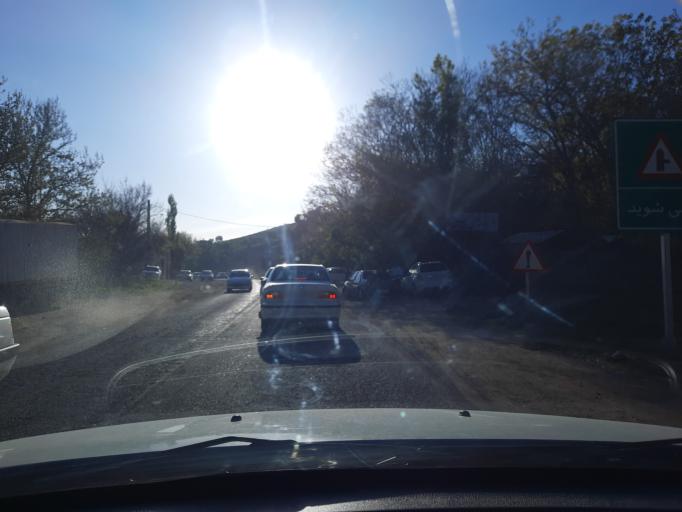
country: IR
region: Qazvin
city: Qazvin
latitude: 36.3447
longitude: 50.1782
